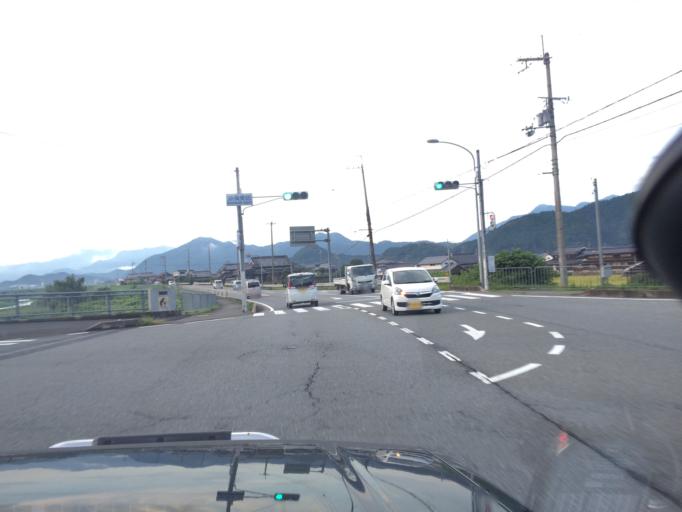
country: JP
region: Hyogo
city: Nishiwaki
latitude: 35.1387
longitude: 135.0271
